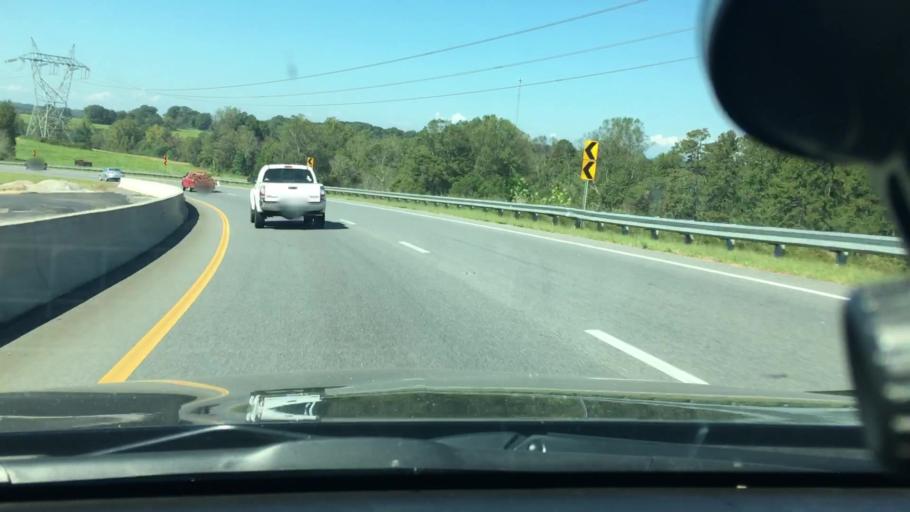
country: US
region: North Carolina
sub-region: Cleveland County
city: Boiling Springs
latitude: 35.2980
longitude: -81.6577
